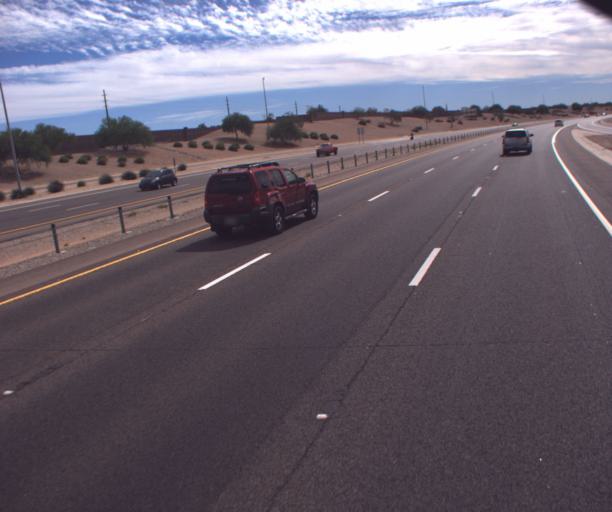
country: US
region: Arizona
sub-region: Maricopa County
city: Gilbert
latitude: 33.3045
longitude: -111.7395
